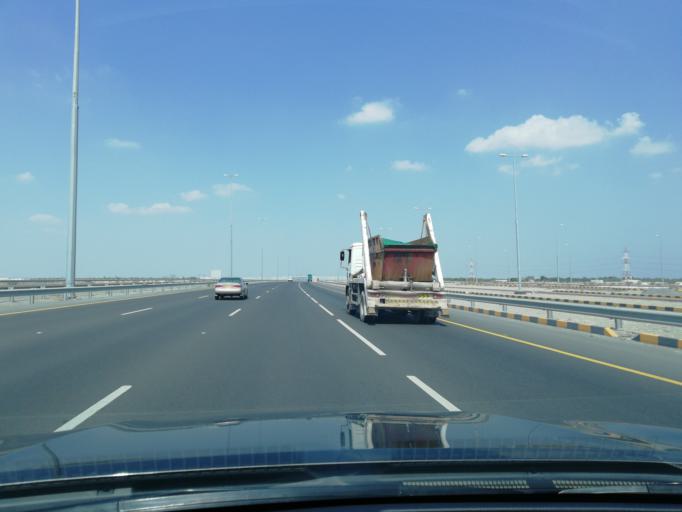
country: OM
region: Al Batinah
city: Barka'
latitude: 23.6298
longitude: 58.0039
